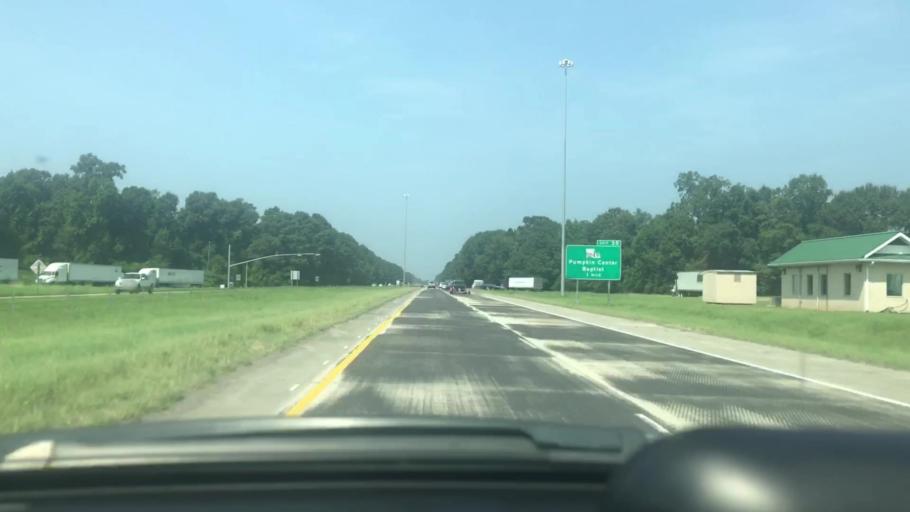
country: US
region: Louisiana
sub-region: Tangipahoa Parish
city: Hammond
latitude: 30.4796
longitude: -90.5210
